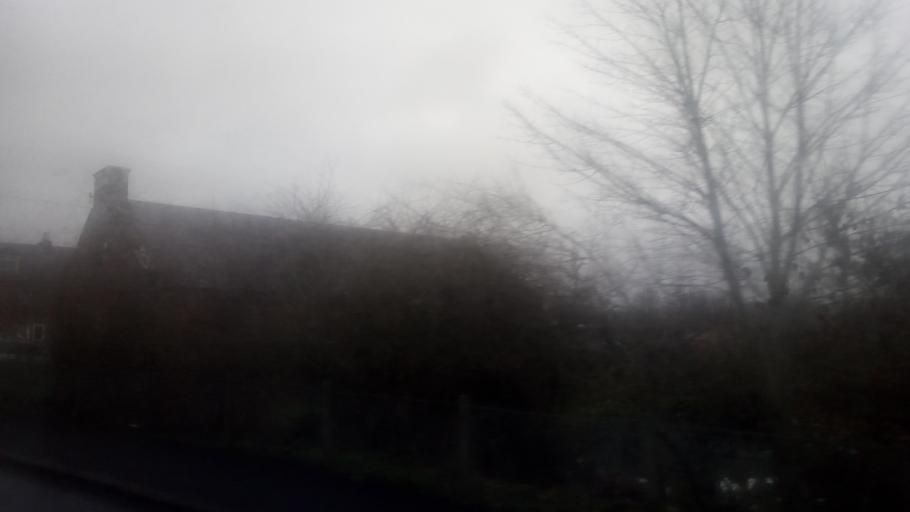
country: GB
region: Scotland
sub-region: The Scottish Borders
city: Newtown St Boswells
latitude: 55.5802
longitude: -2.6745
